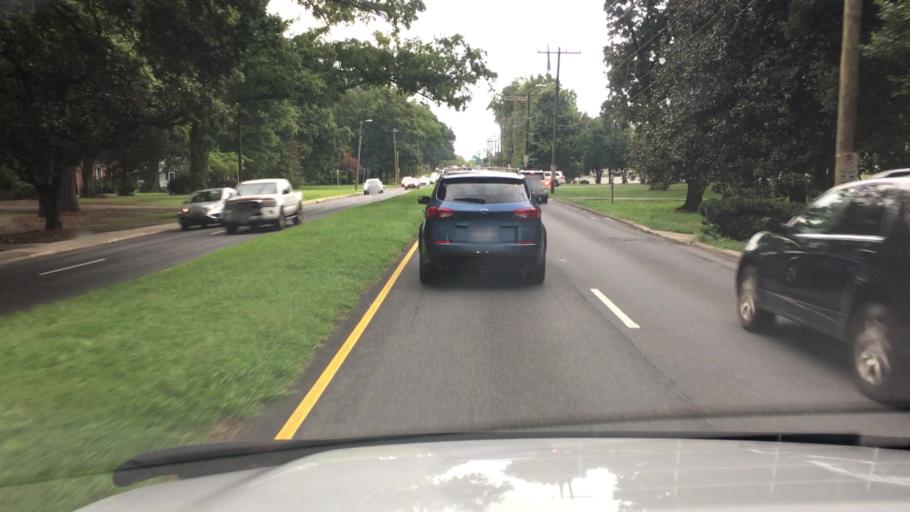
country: US
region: North Carolina
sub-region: Mecklenburg County
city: Charlotte
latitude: 35.1736
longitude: -80.8119
